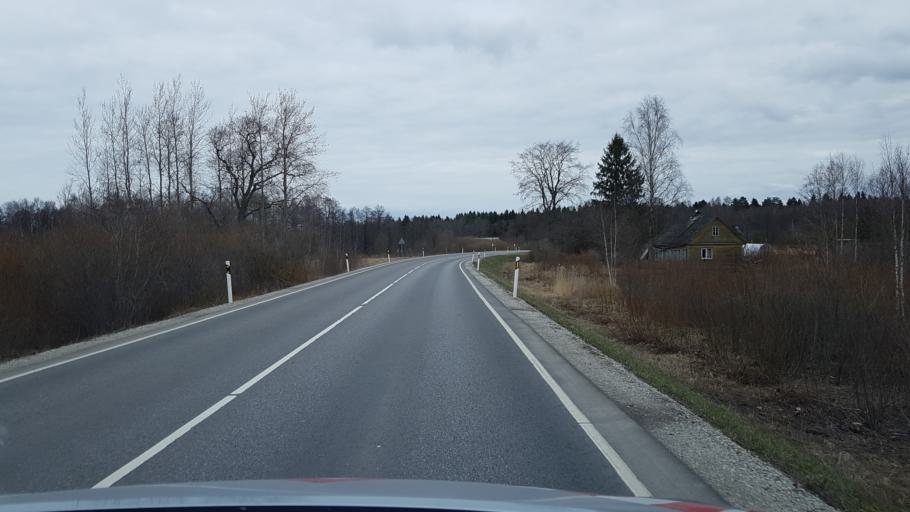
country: EE
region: Ida-Virumaa
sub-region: Narva-Joesuu linn
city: Narva-Joesuu
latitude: 59.4099
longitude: 28.0681
